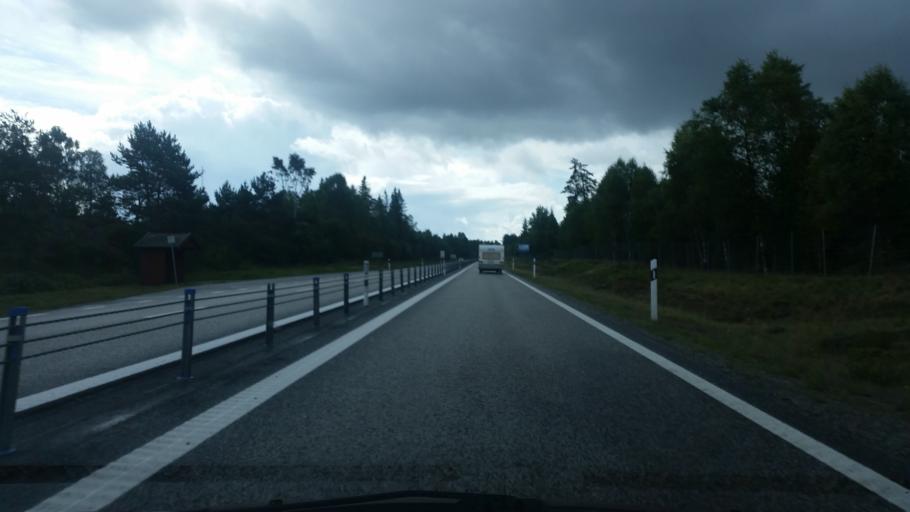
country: SE
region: Joenkoeping
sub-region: Gislaveds Kommun
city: Gislaved
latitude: 57.3360
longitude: 13.5488
